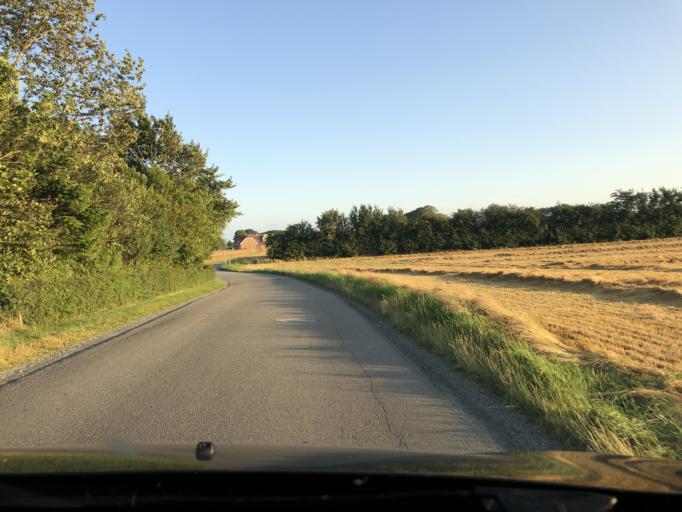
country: DK
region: South Denmark
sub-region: Vejle Kommune
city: Brejning
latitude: 55.6431
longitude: 9.7018
